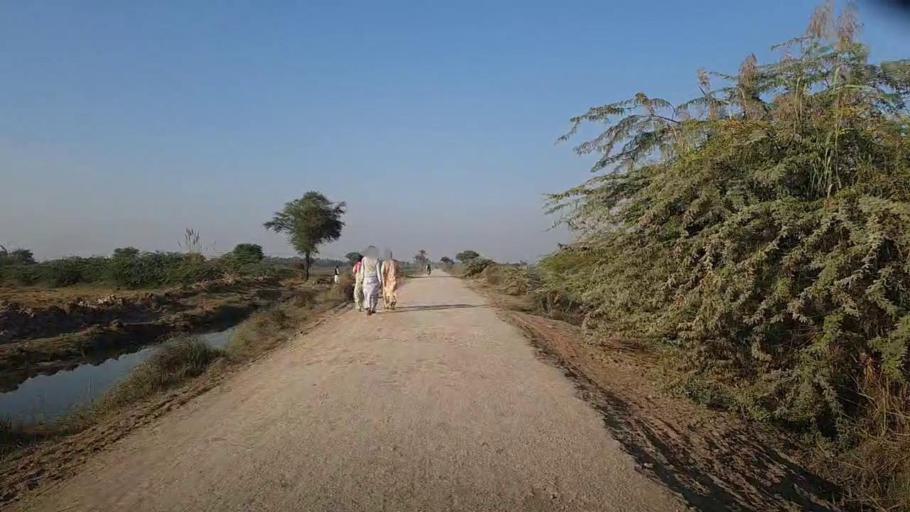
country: PK
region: Sindh
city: Ranipur
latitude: 27.2608
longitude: 68.5121
